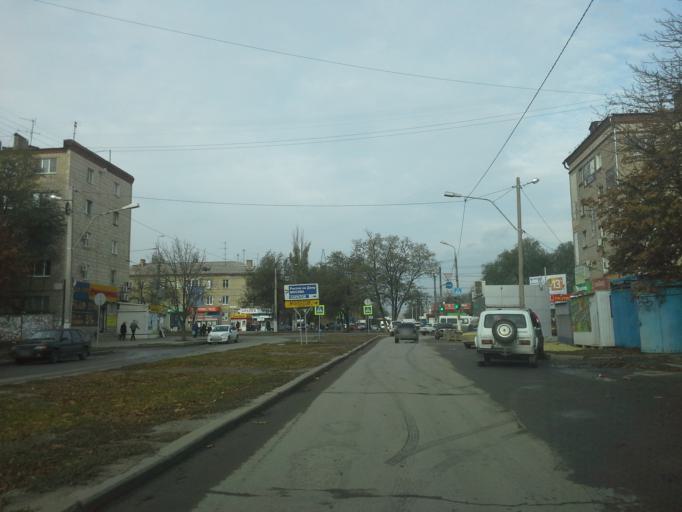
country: RU
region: Volgograd
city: Vodstroy
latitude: 48.7836
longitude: 44.5652
